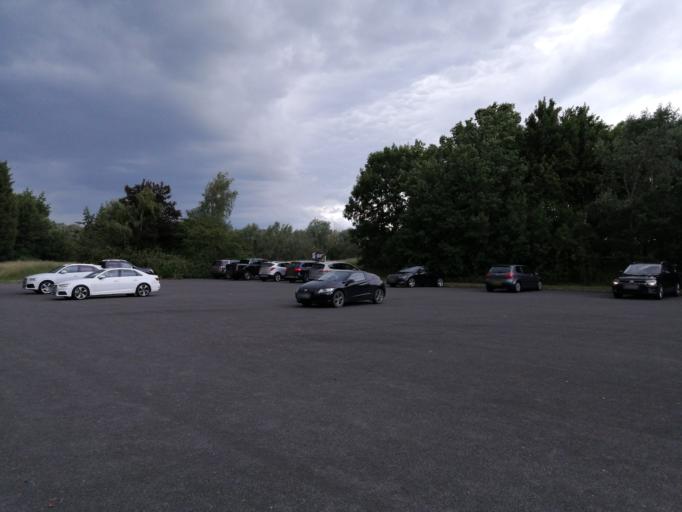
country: GB
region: England
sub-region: Cambridgeshire
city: Buckden
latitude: 52.2844
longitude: -0.2978
